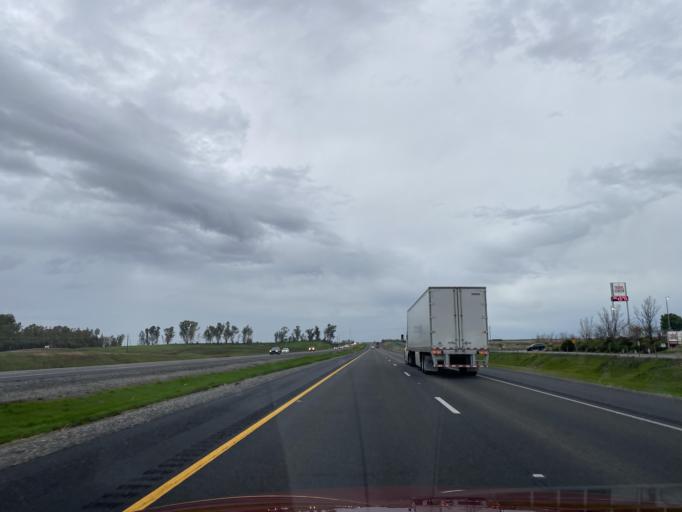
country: US
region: California
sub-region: Tehama County
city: Corning
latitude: 39.8734
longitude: -122.2002
